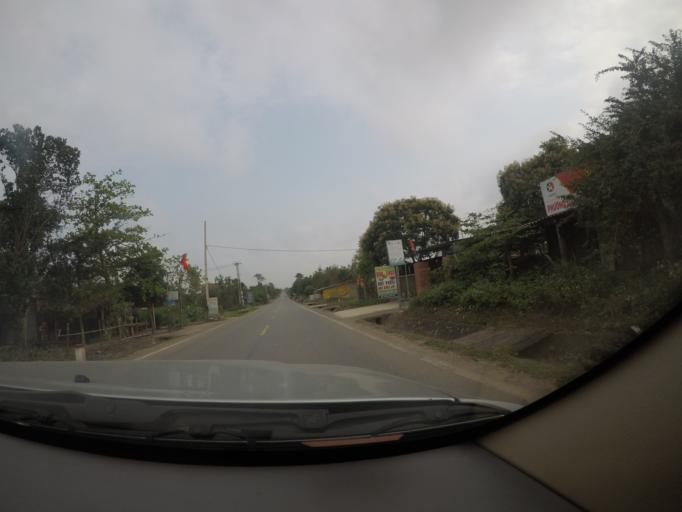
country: VN
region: Quang Binh
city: Kwang Binh
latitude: 17.4805
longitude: 106.5465
